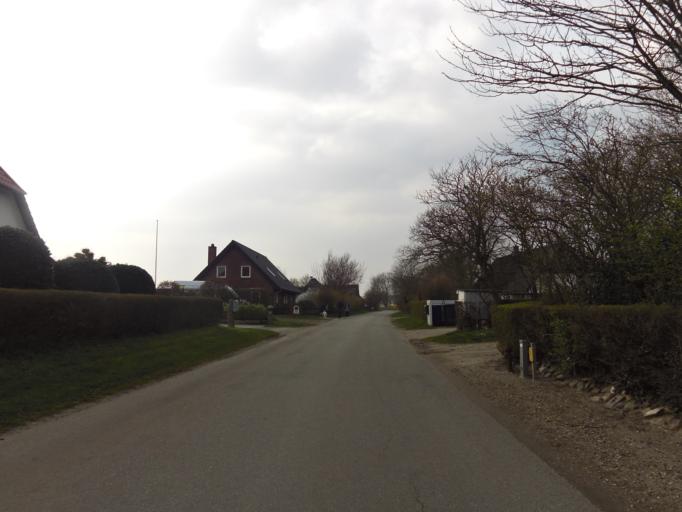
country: DK
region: South Denmark
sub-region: Esbjerg Kommune
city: Ribe
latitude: 55.3542
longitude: 8.7338
